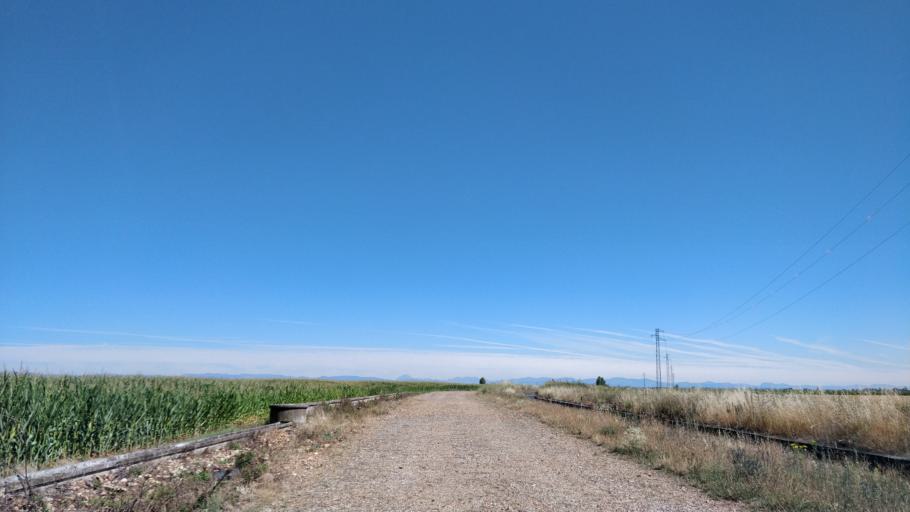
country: ES
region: Castille and Leon
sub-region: Provincia de Leon
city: Bustillo del Paramo
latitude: 42.4314
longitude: -5.8220
